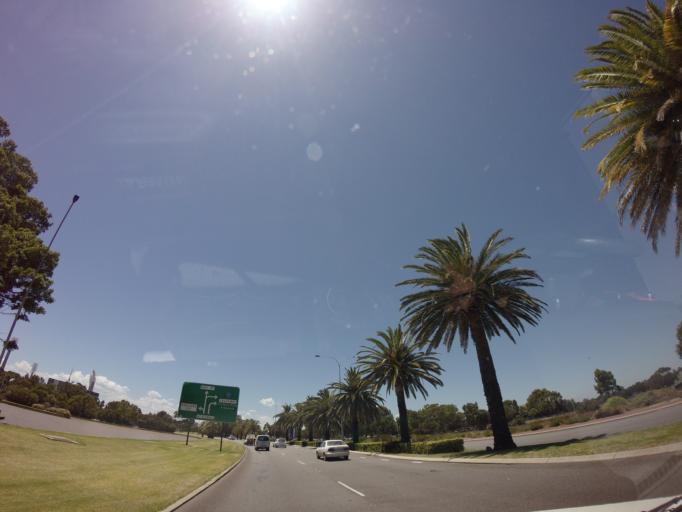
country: AU
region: Western Australia
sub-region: City of Perth
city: East Perth
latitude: -31.9639
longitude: 115.8762
